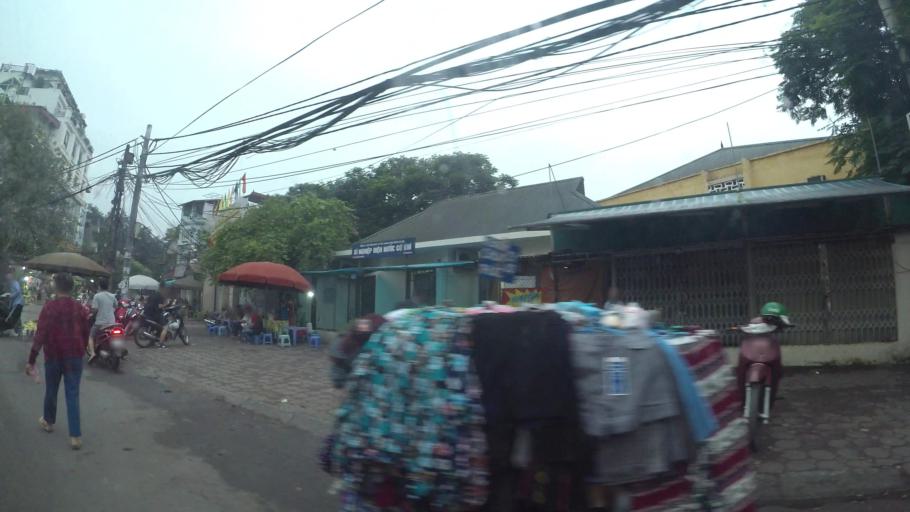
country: VN
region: Ha Noi
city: Hanoi
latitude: 21.0202
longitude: 105.8382
